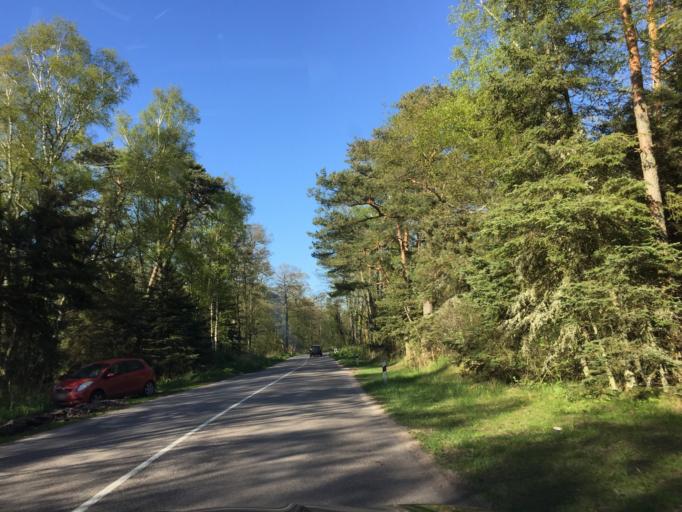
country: LT
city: Nida
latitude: 55.1911
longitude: 20.8593
